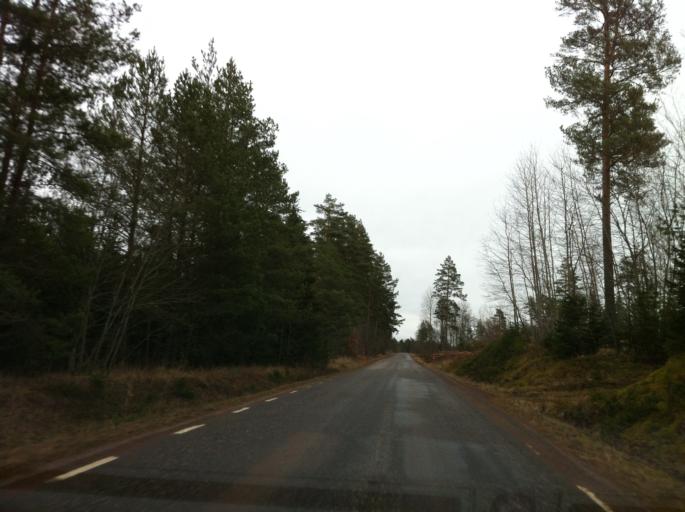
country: SE
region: Kalmar
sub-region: Vasterviks Kommun
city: Overum
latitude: 57.9020
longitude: 16.0950
